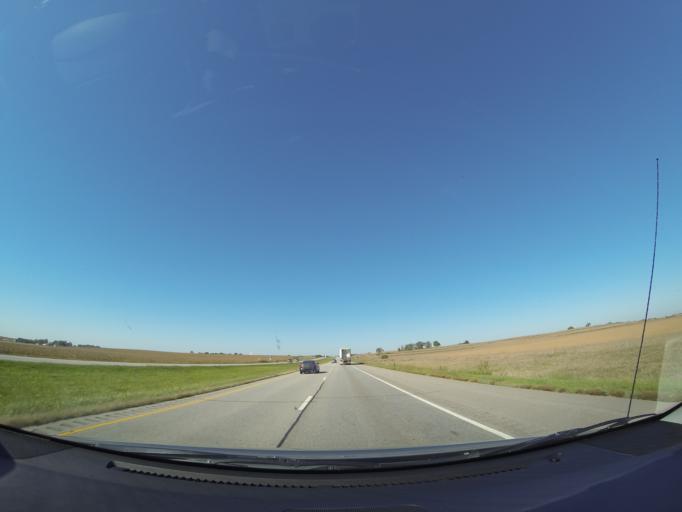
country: US
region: Nebraska
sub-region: Seward County
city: Milford
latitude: 40.8223
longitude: -97.0872
